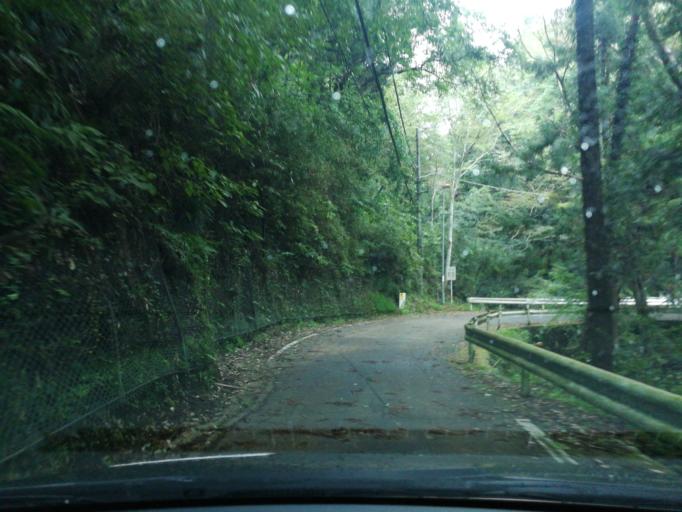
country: JP
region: Yamanashi
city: Uenohara
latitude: 35.6126
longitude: 139.2209
